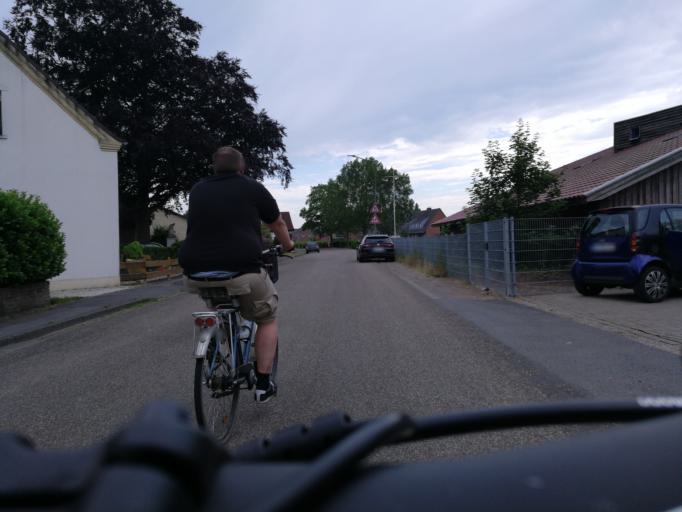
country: DE
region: North Rhine-Westphalia
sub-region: Regierungsbezirk Dusseldorf
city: Kleve
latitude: 51.8256
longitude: 6.1409
